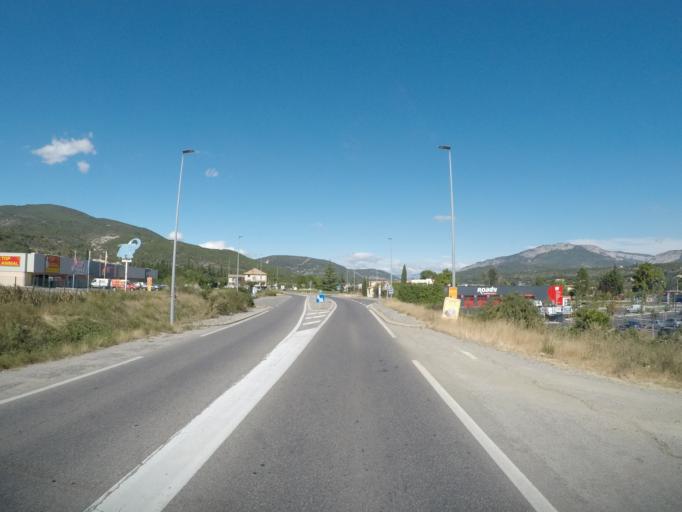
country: FR
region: Provence-Alpes-Cote d'Azur
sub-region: Departement des Alpes-de-Haute-Provence
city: Peipin
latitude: 44.1388
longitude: 5.9683
